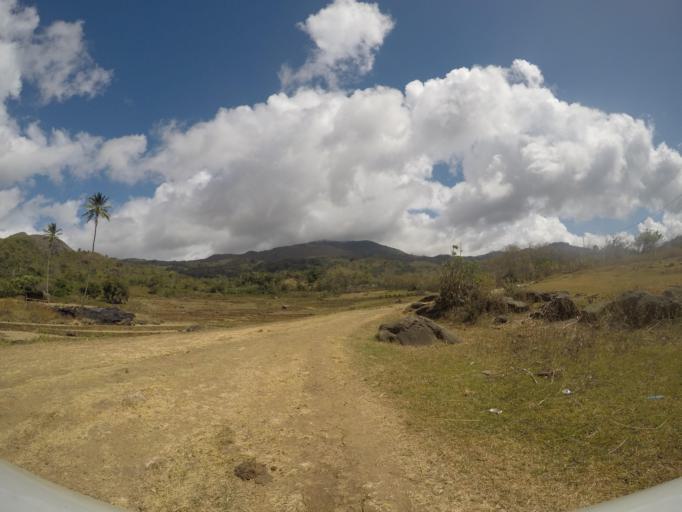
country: TL
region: Lautem
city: Lospalos
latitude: -8.5294
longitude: 126.8005
